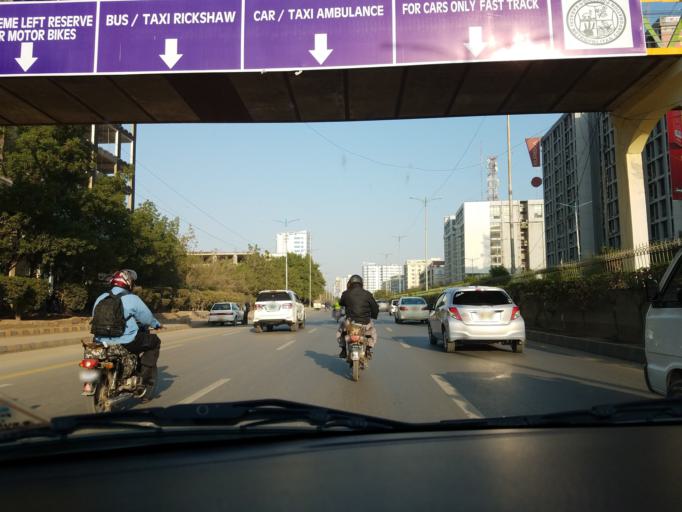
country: PK
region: Sindh
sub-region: Karachi District
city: Karachi
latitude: 24.8621
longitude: 67.0694
